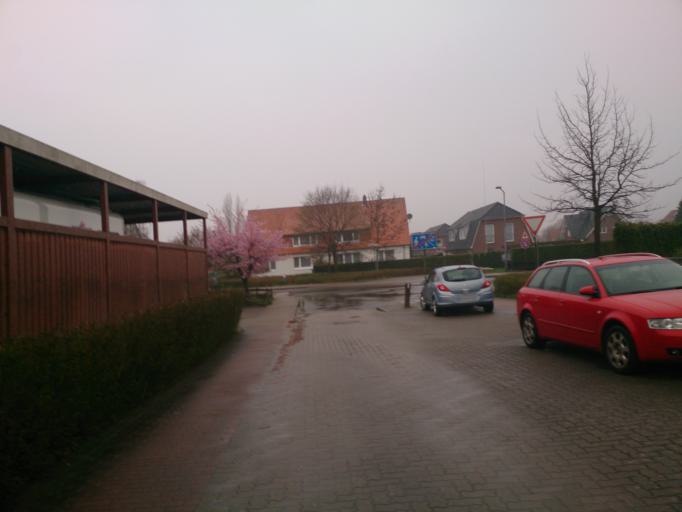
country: DE
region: Lower Saxony
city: Neu Wulmstorf
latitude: 53.4694
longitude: 9.7963
